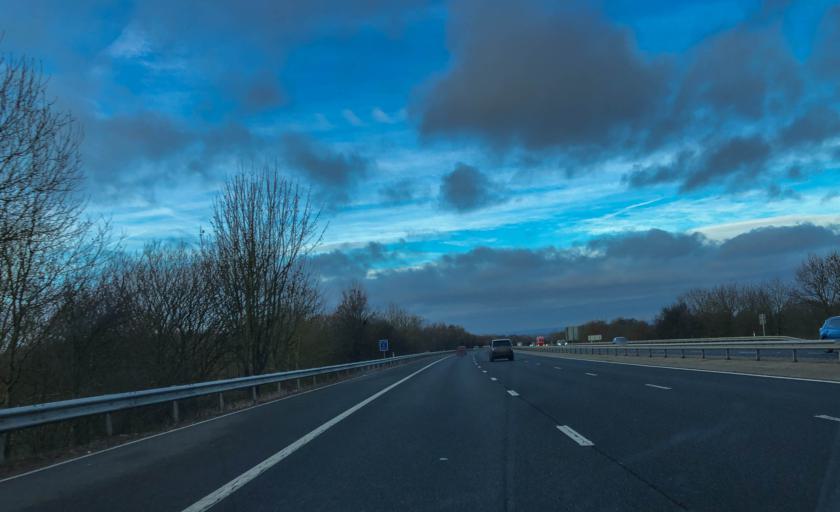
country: GB
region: England
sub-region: Kent
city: Borough Green
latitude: 51.3277
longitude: 0.2732
